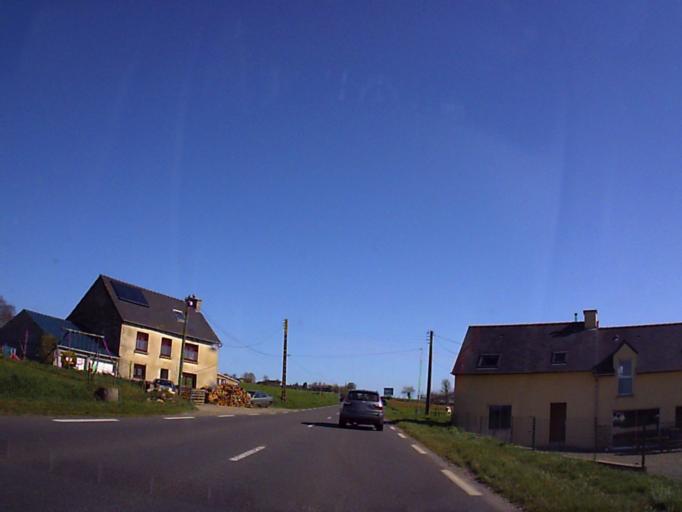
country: FR
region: Brittany
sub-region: Departement d'Ille-et-Vilaine
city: Quedillac
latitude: 48.2567
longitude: -2.1667
